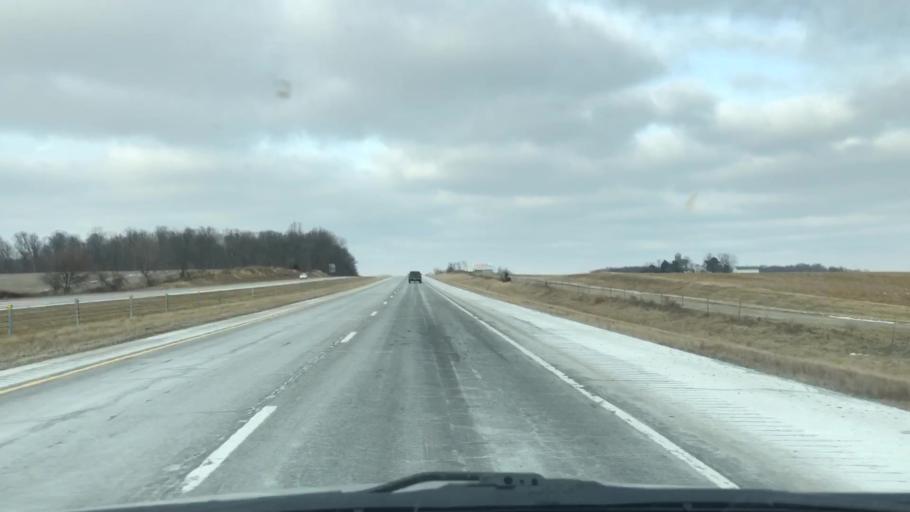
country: US
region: Indiana
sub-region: Steuben County
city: Angola
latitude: 41.5431
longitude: -85.0560
